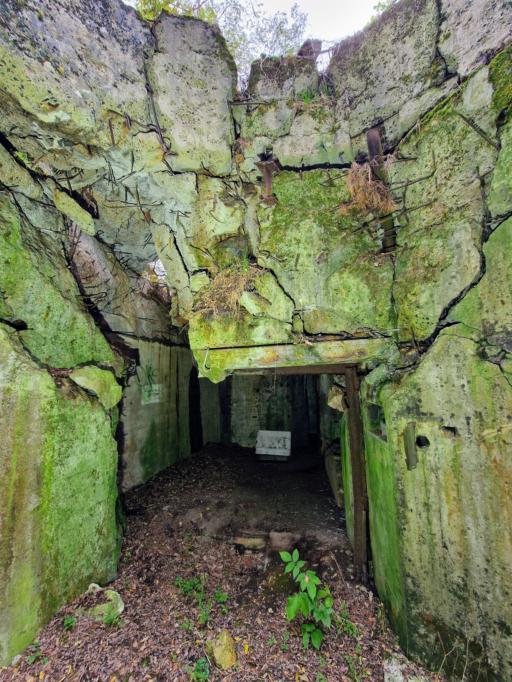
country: PL
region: Lubusz
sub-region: Powiat swiebodzinski
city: Lubrza
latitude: 52.3477
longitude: 15.4807
